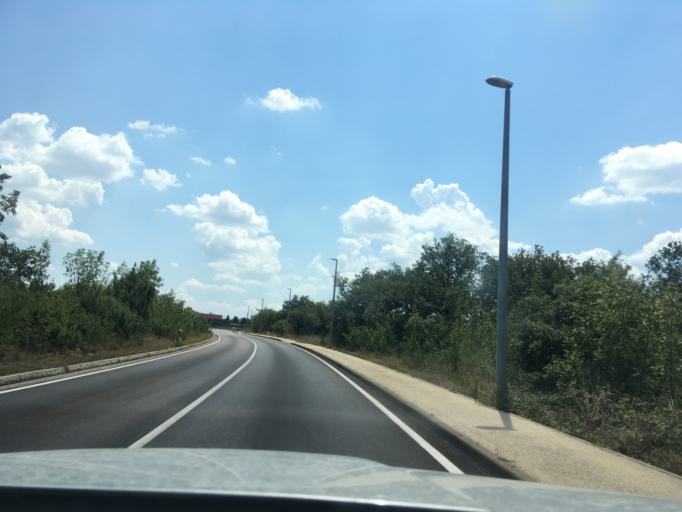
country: HR
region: Zadarska
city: Policnik
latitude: 44.1540
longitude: 15.3143
